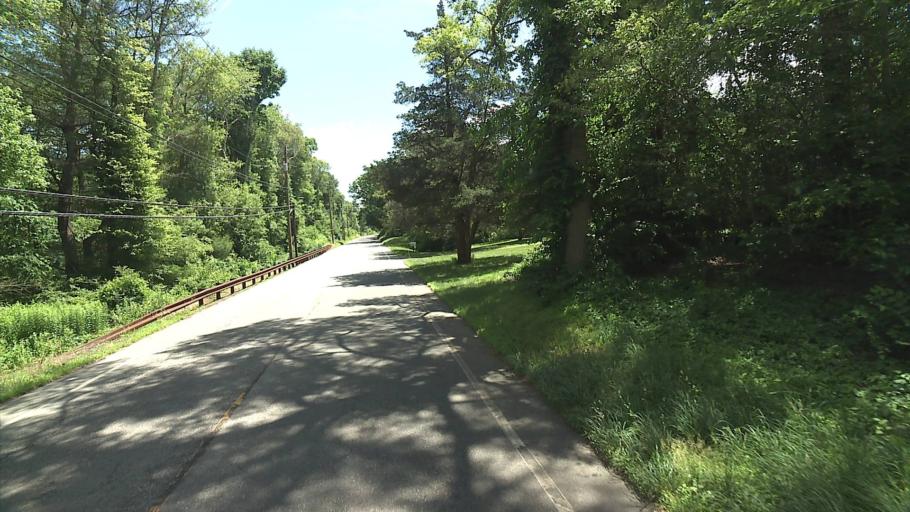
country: US
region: Rhode Island
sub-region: Washington County
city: Ashaway
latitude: 41.4336
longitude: -71.8374
